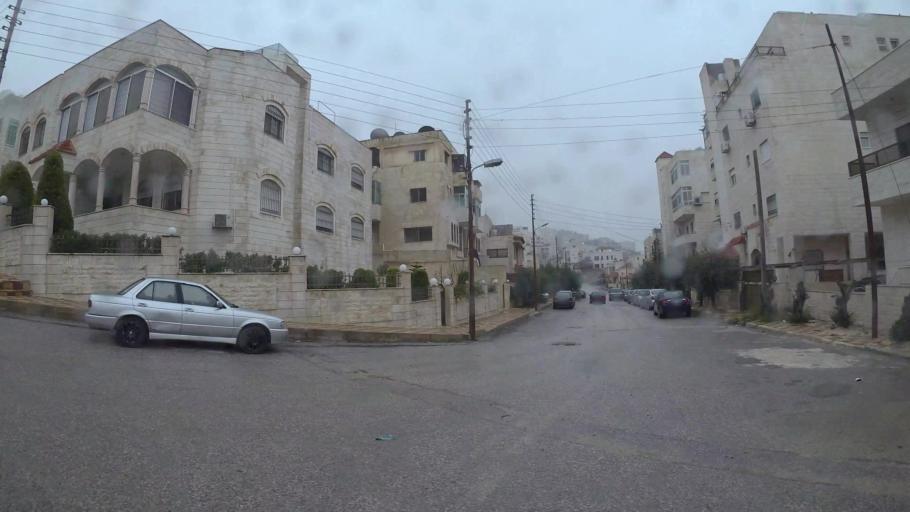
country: JO
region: Amman
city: Al Jubayhah
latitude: 32.0357
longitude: 35.8526
